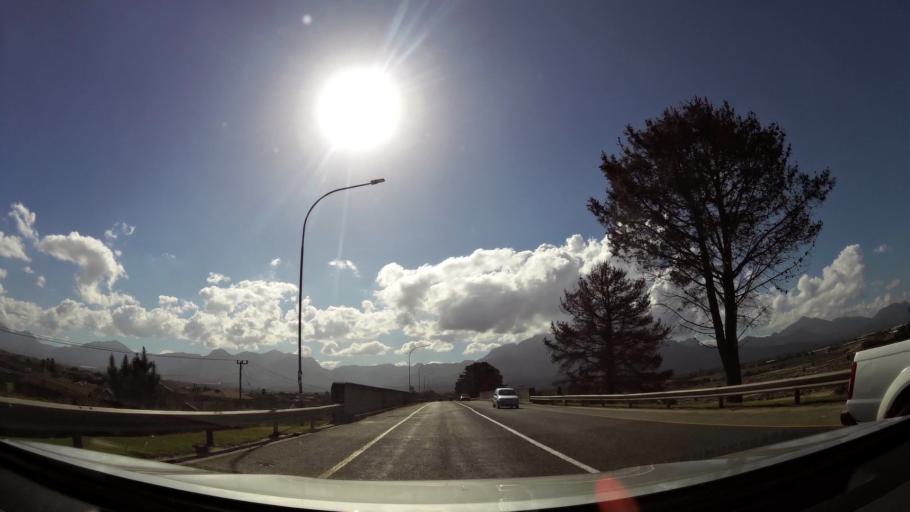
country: ZA
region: Western Cape
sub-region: Eden District Municipality
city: George
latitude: -33.9862
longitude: 22.4415
